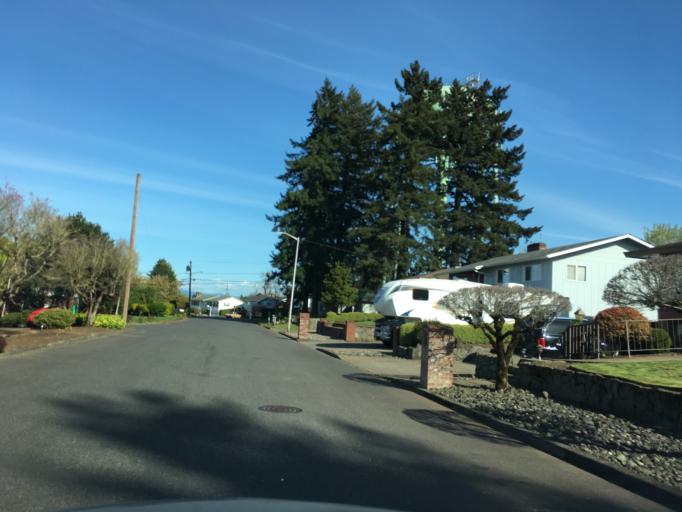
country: US
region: Oregon
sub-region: Multnomah County
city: Lents
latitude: 45.5455
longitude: -122.5259
